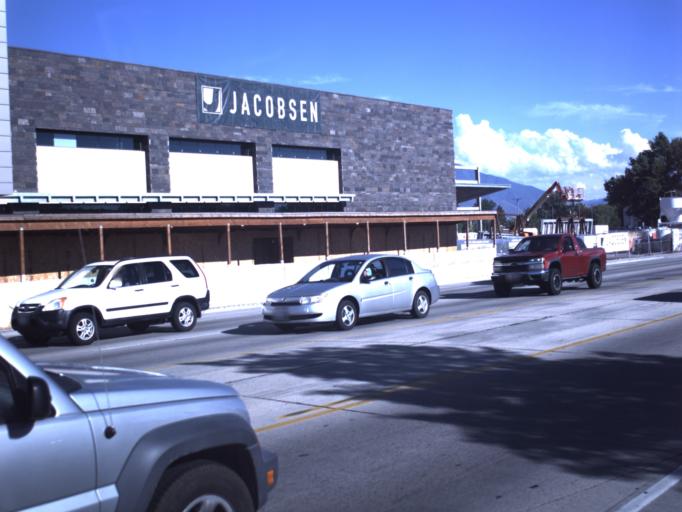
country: US
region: Utah
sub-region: Utah County
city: Provo
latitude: 40.2475
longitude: -111.6675
